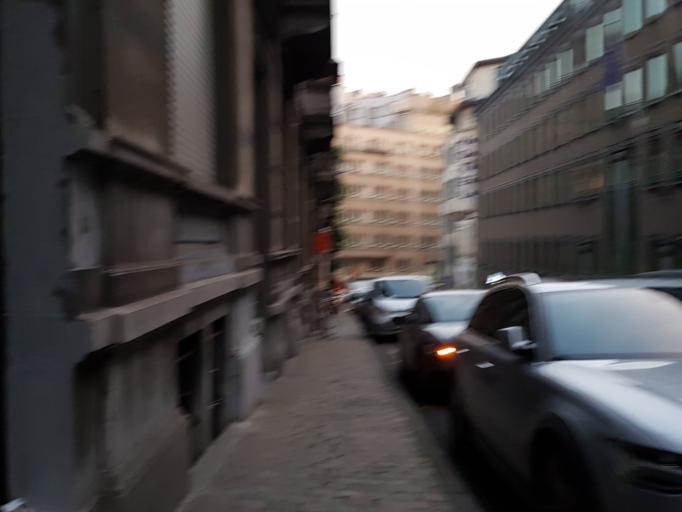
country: BE
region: Brussels Capital
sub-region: Bruxelles-Capitale
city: Brussels
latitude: 50.8284
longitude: 4.3652
